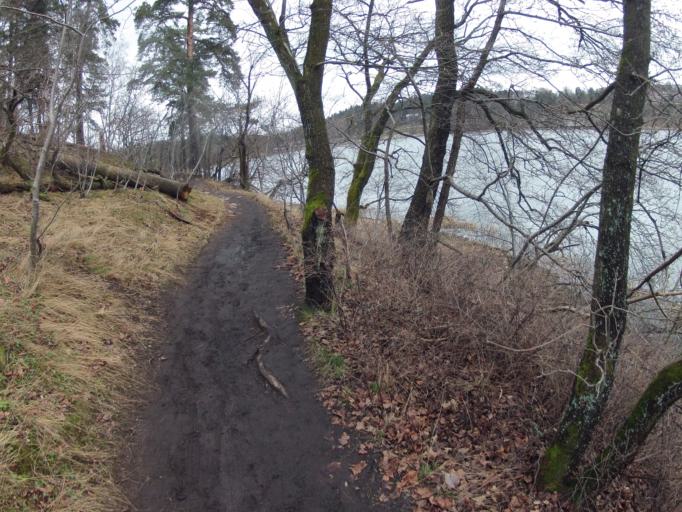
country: SE
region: Stockholm
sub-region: Norrtalje Kommun
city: Bergshamra
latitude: 59.3753
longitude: 18.0208
